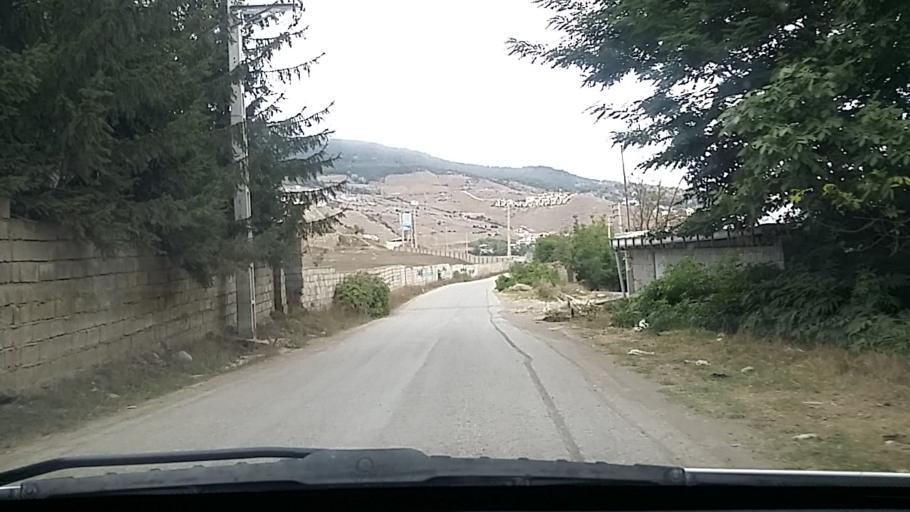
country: IR
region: Mazandaran
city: `Abbasabad
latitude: 36.5116
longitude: 51.1613
